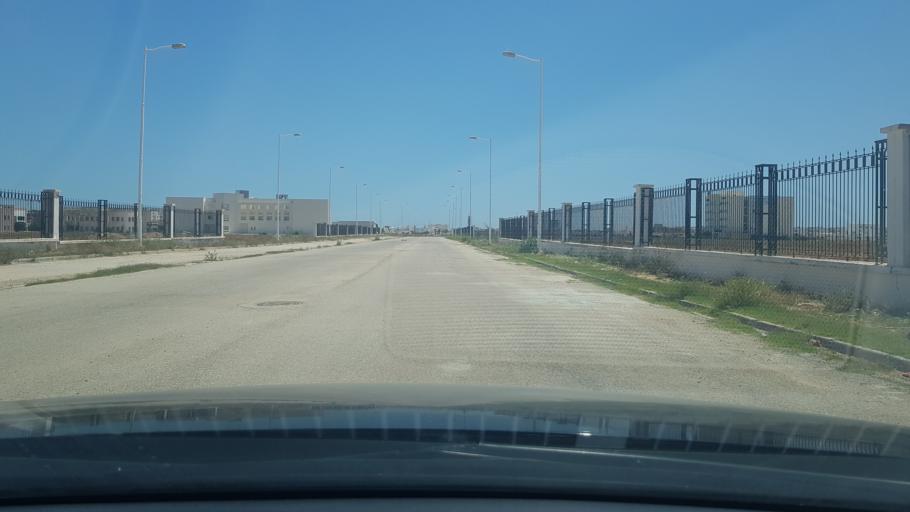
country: TN
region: Safaqis
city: Al Qarmadah
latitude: 34.8376
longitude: 10.7511
